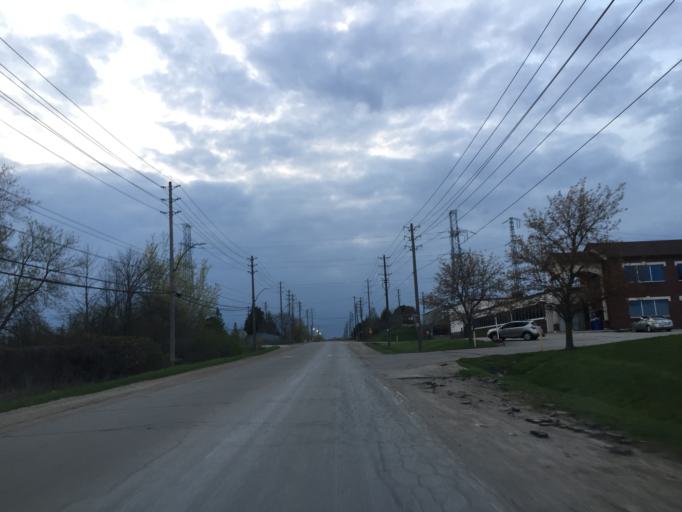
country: CA
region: Ontario
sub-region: Wellington County
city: Guelph
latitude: 43.5520
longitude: -80.2826
